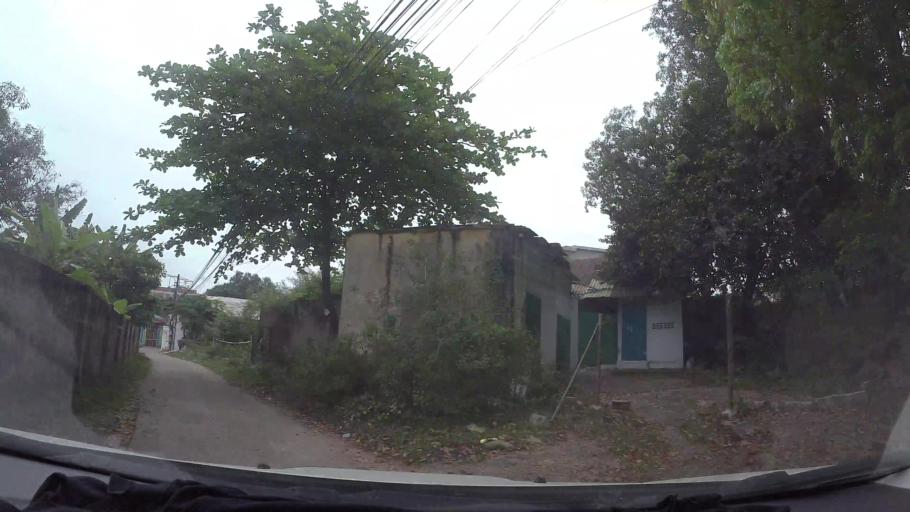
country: VN
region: Da Nang
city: Lien Chieu
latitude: 16.0673
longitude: 108.1444
